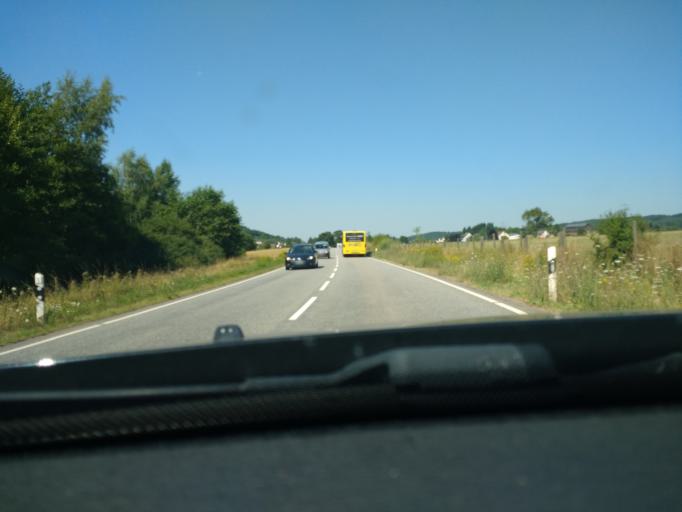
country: DE
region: Rheinland-Pfalz
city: Neuerburg
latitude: 50.0004
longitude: 6.9631
